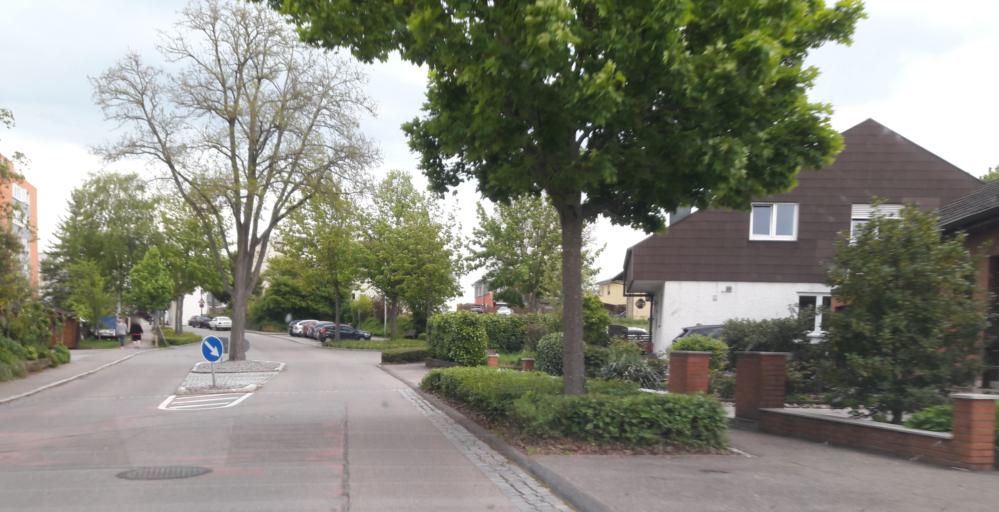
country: DE
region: Baden-Wuerttemberg
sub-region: Regierungsbezirk Stuttgart
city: Untereisesheim
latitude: 49.2086
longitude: 9.1967
